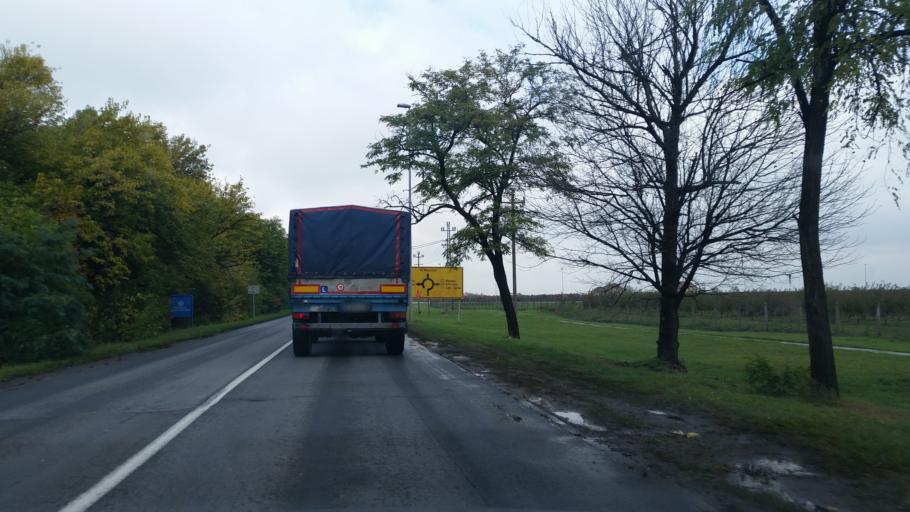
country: RS
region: Autonomna Pokrajina Vojvodina
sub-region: Srednjebanatski Okrug
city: Zrenjanin
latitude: 45.3993
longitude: 20.3774
